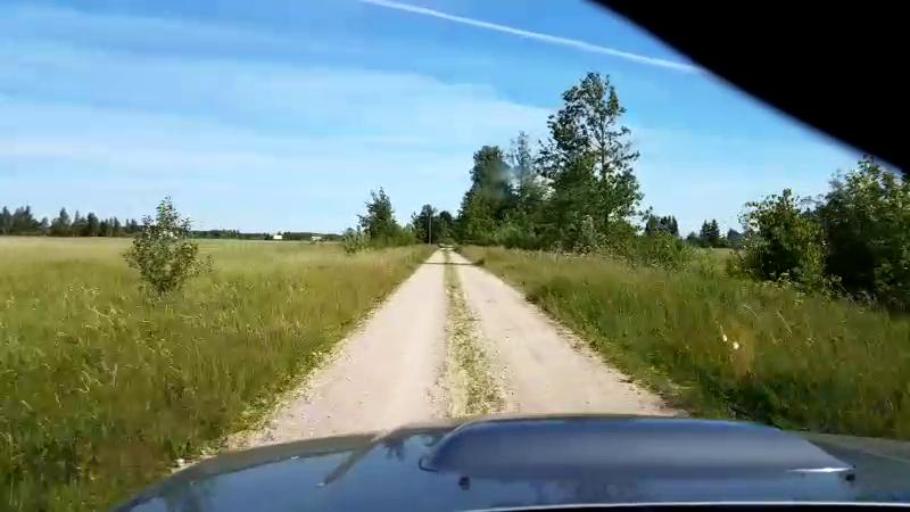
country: EE
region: Paernumaa
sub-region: Sauga vald
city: Sauga
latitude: 58.4867
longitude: 24.5310
